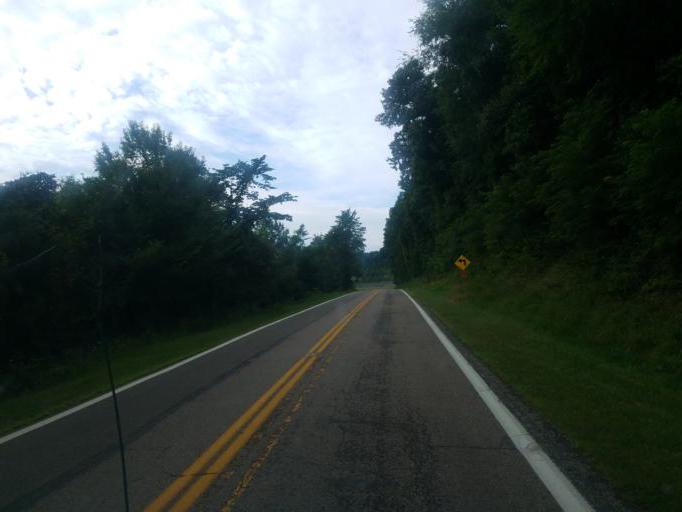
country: US
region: Ohio
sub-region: Knox County
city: Oak Hill
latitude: 40.3511
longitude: -82.0823
